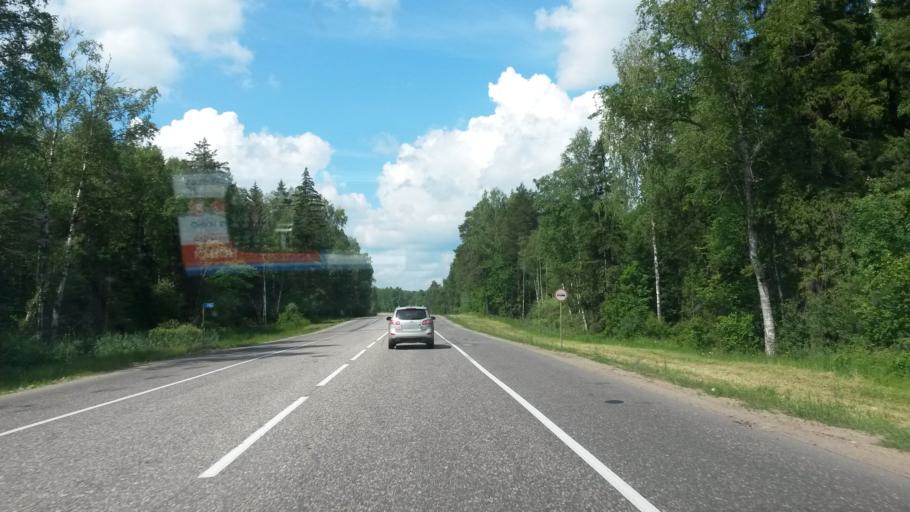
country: RU
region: Jaroslavl
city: Pereslavl'-Zalesskiy
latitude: 56.8701
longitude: 38.9787
